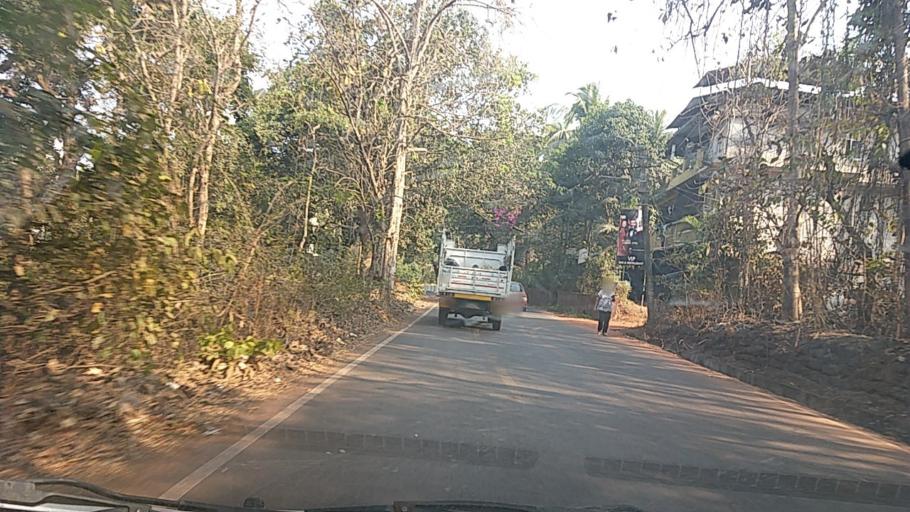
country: IN
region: Goa
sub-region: North Goa
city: Goa Velha
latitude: 15.4786
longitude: 73.9247
